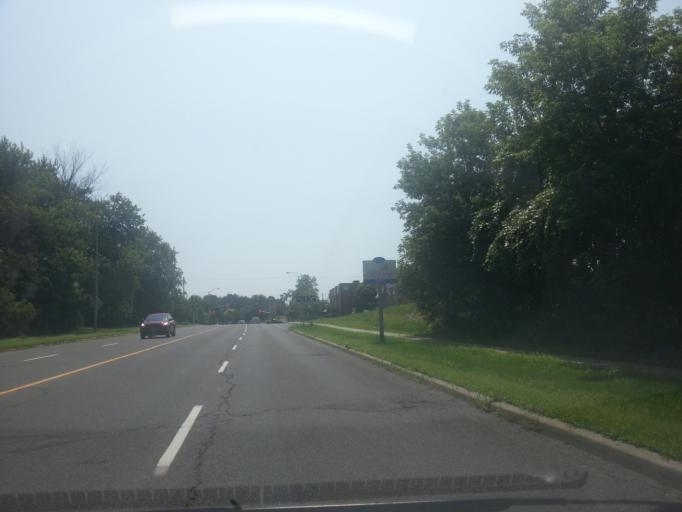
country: CA
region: Quebec
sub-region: Outaouais
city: Gatineau
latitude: 45.4700
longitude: -75.5316
